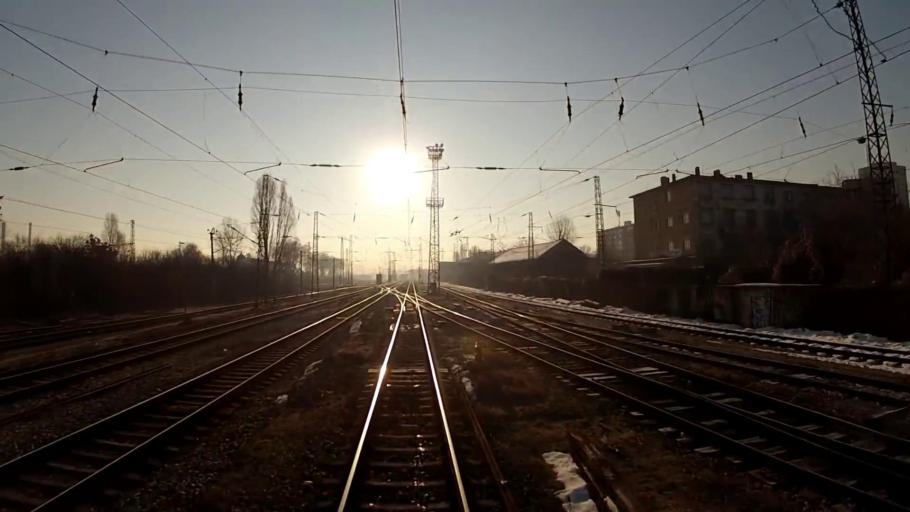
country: BG
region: Sofia-Capital
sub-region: Stolichna Obshtina
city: Sofia
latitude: 42.7238
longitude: 23.2926
